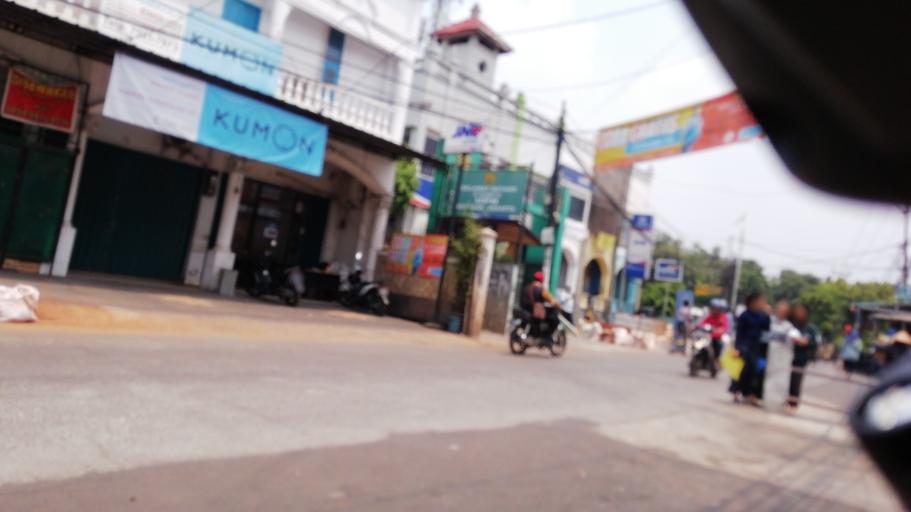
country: ID
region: West Java
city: Pamulang
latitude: -6.3156
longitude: 106.7959
